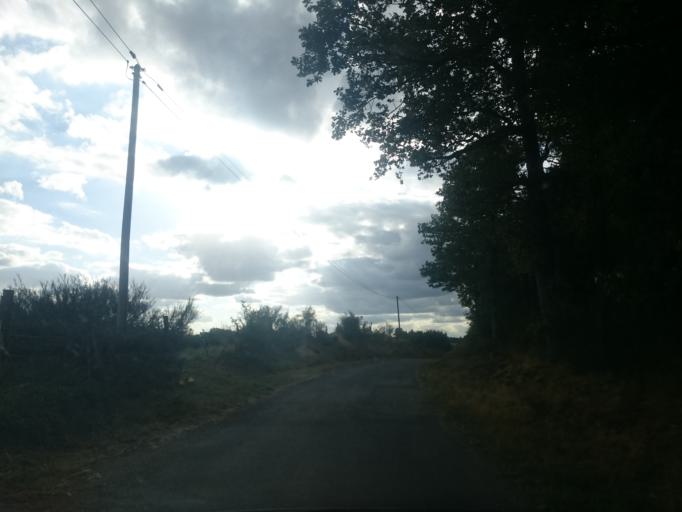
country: FR
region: Auvergne
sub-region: Departement du Cantal
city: Saint-Mamet-la-Salvetat
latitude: 44.8576
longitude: 2.2630
